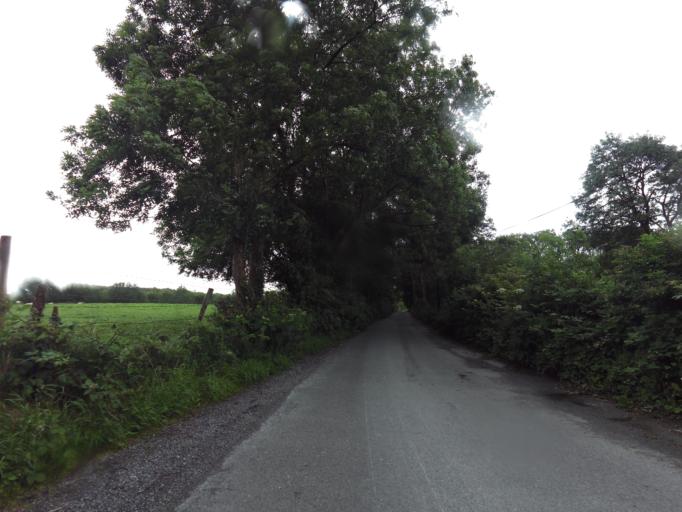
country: IE
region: Connaught
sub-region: County Galway
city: Athenry
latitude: 53.2843
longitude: -8.6878
